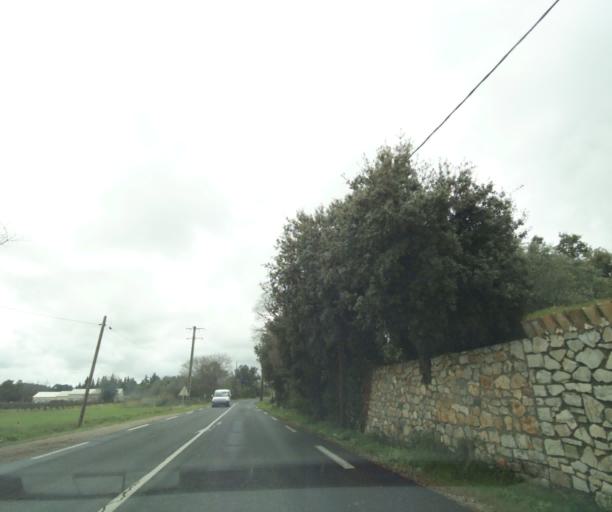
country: FR
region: Languedoc-Roussillon
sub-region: Departement de l'Herault
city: Cournonsec
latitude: 43.5444
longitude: 3.7041
